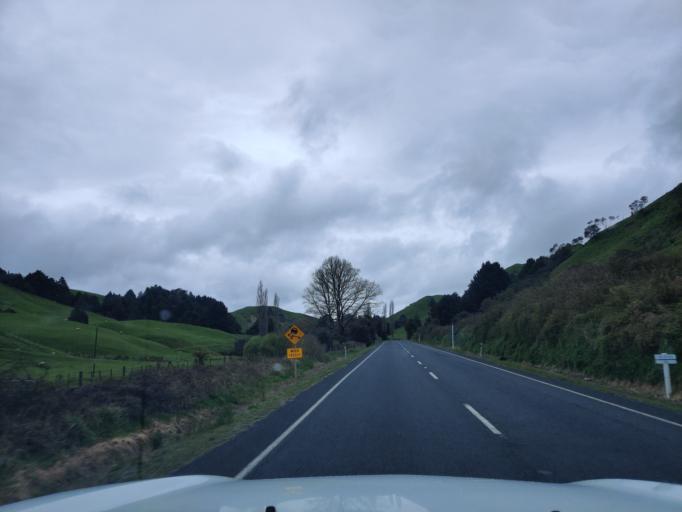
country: NZ
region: Waikato
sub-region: Otorohanga District
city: Otorohanga
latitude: -38.5710
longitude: 175.2070
